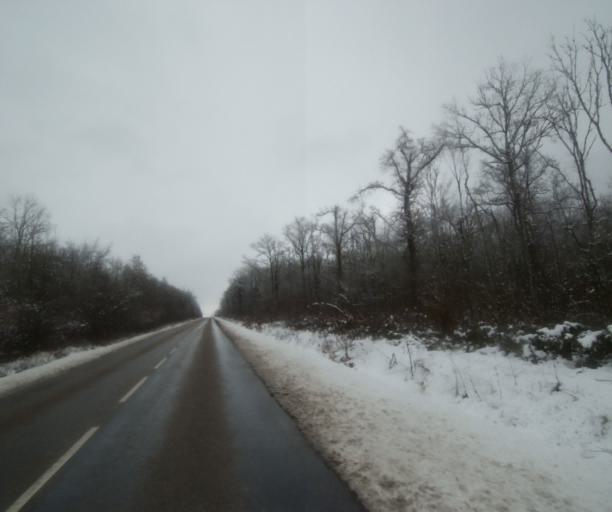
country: FR
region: Champagne-Ardenne
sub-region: Departement de la Haute-Marne
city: Wassy
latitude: 48.4947
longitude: 4.9139
